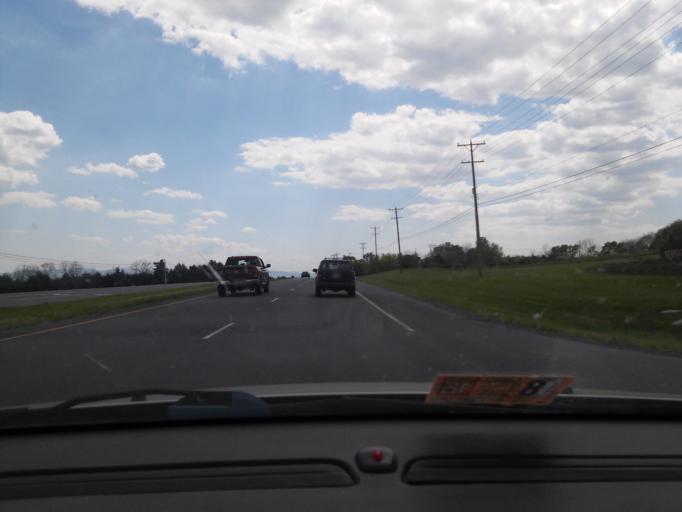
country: US
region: Virginia
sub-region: Frederick County
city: Stephens City
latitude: 39.0387
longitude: -78.1502
